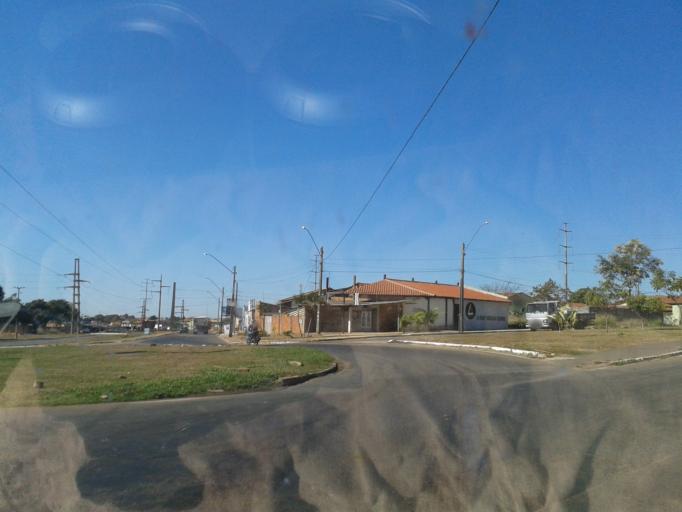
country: BR
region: Goias
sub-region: Aparecida De Goiania
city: Aparecida de Goiania
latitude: -16.7765
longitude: -49.2927
